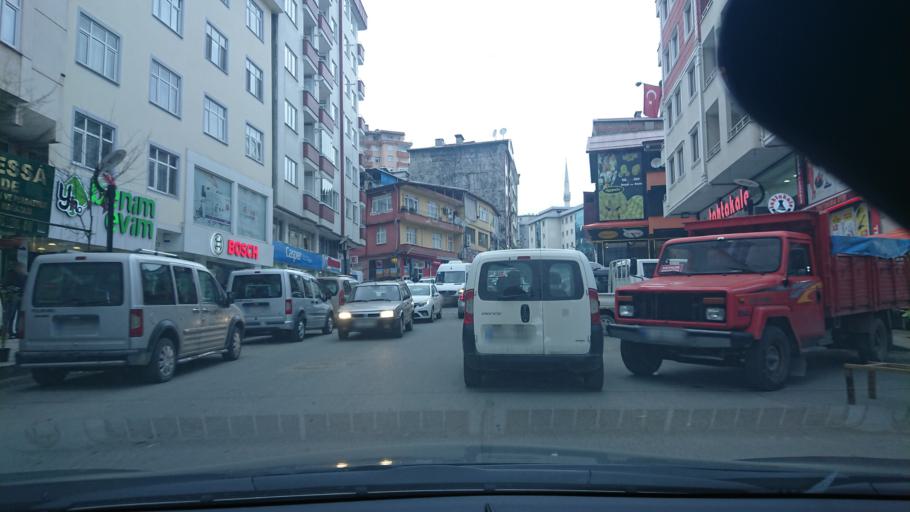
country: TR
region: Rize
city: Rize
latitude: 41.0269
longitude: 40.5146
